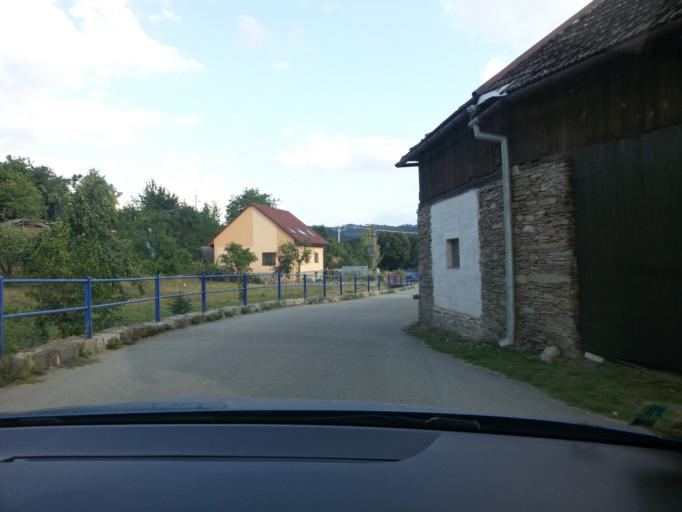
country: CZ
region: South Moravian
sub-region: Okres Brno-Venkov
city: Lomnice
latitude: 49.4609
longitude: 16.4270
